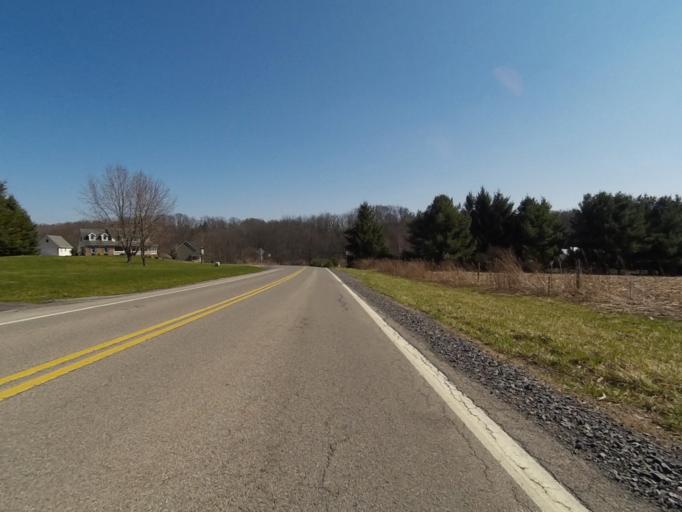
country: US
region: Pennsylvania
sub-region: Centre County
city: Park Forest Village
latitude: 40.8153
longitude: -77.9588
